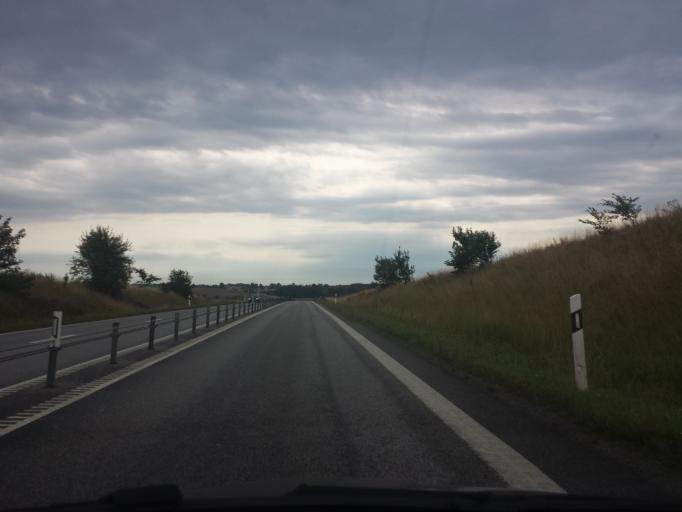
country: SE
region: Skane
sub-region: Ystads Kommun
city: Ystad
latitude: 55.4666
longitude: 13.7125
